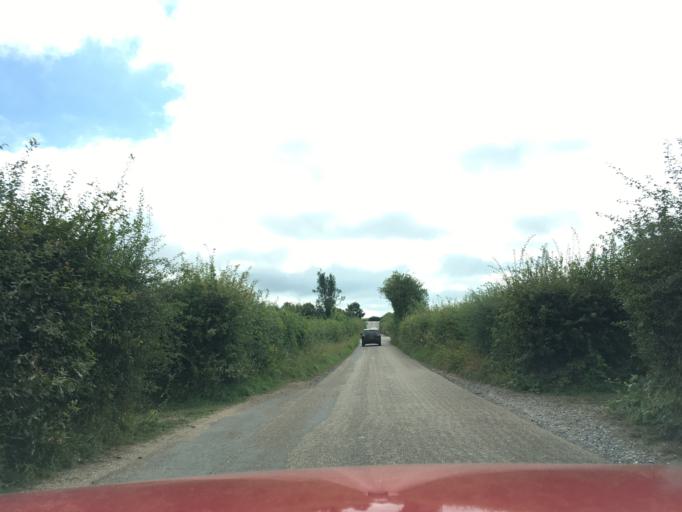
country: GB
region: England
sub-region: Kent
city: Cranbrook
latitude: 51.1120
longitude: 0.5727
